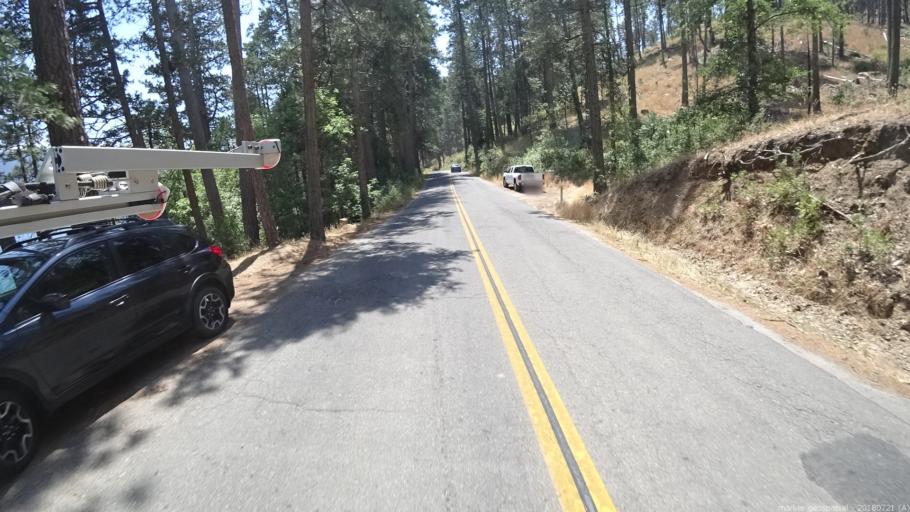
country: US
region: California
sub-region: Madera County
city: Oakhurst
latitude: 37.3122
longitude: -119.5561
